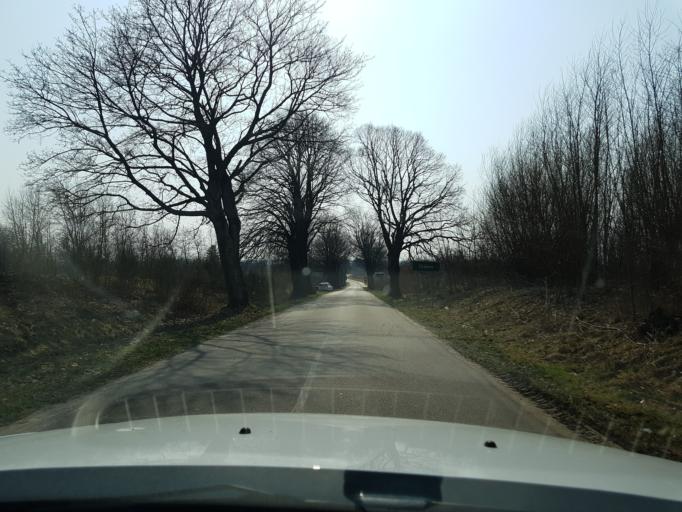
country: PL
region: West Pomeranian Voivodeship
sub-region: Powiat koszalinski
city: Sianow
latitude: 54.2544
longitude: 16.3106
